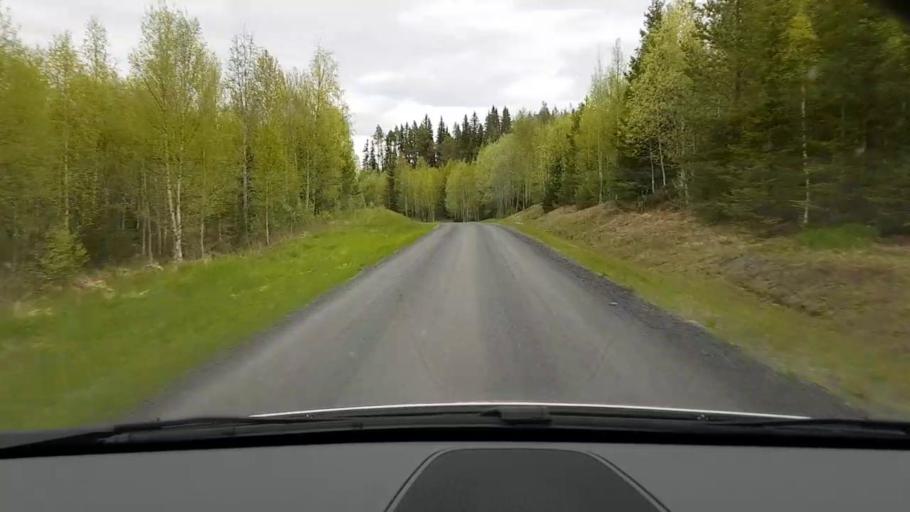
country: SE
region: Jaemtland
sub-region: Krokoms Kommun
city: Krokom
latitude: 63.2979
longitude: 14.3949
